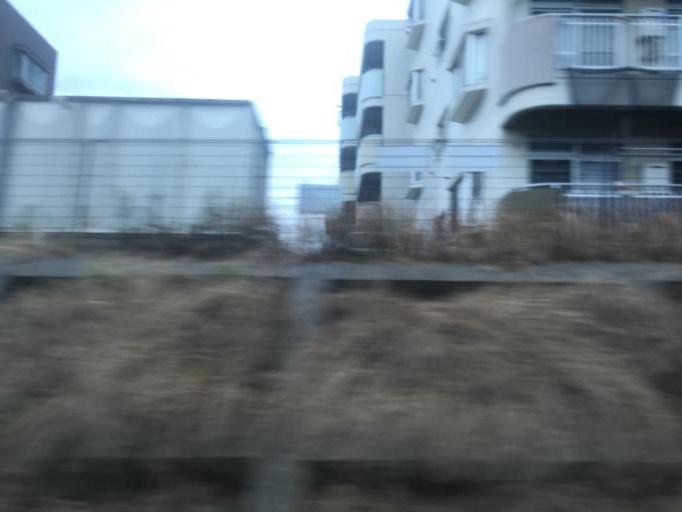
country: JP
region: Saitama
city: Ageoshimo
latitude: 35.9190
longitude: 139.5702
